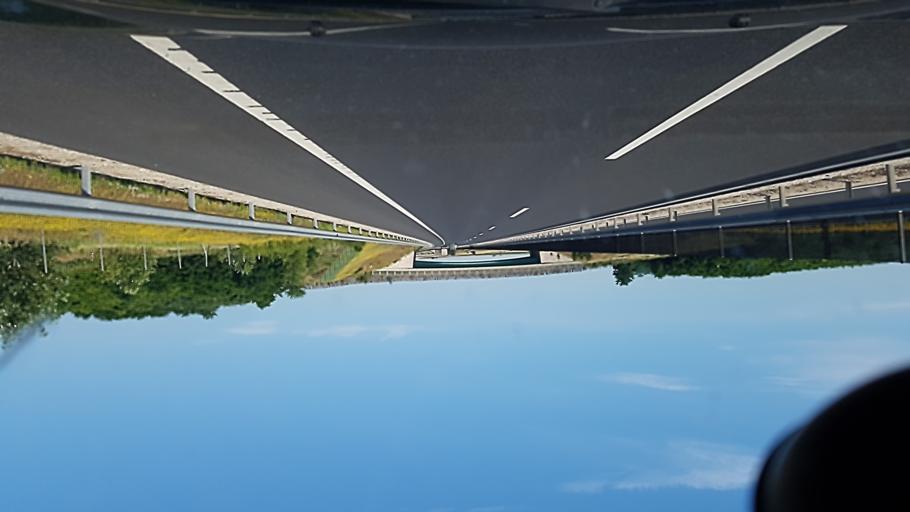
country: HU
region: Tolna
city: Tengelic
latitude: 46.4912
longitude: 18.7562
